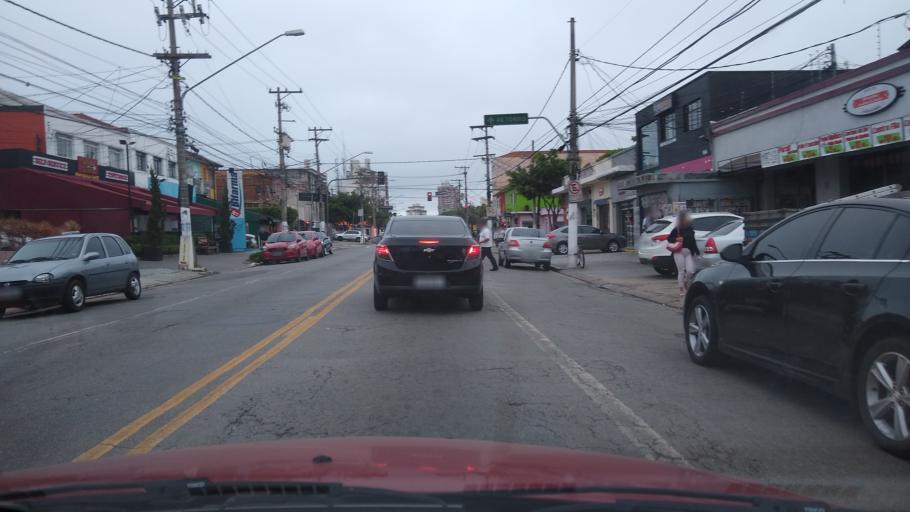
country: BR
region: Sao Paulo
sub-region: Sao Caetano Do Sul
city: Sao Caetano do Sul
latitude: -23.6160
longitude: -46.6177
